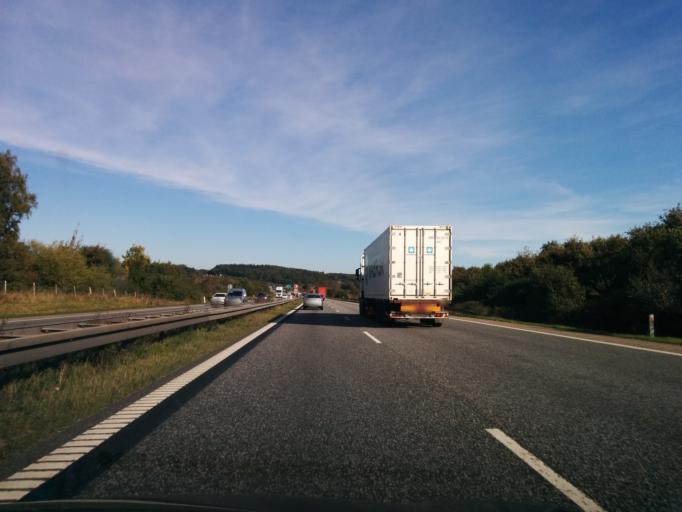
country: DK
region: Central Jutland
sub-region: Horsens Kommune
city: Horsens
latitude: 55.8881
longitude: 9.7969
